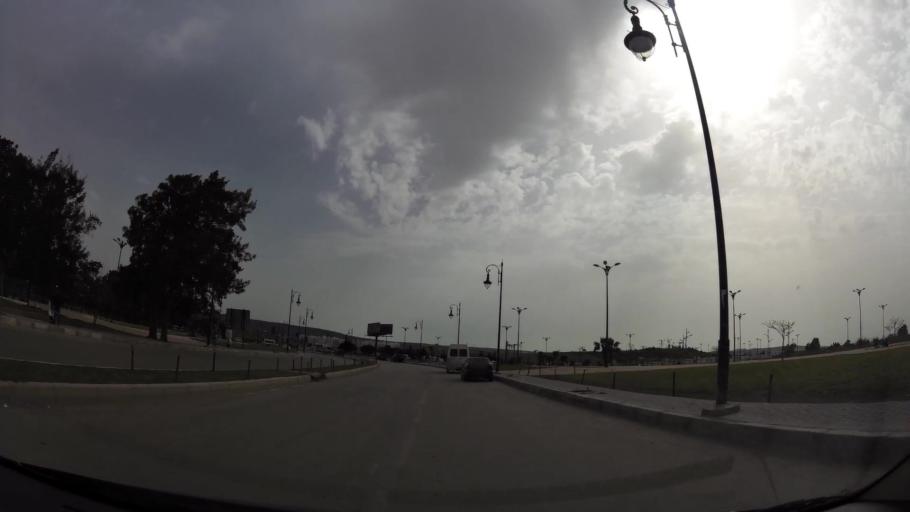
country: MA
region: Tanger-Tetouan
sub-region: Tanger-Assilah
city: Boukhalef
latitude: 35.7301
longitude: -5.8830
